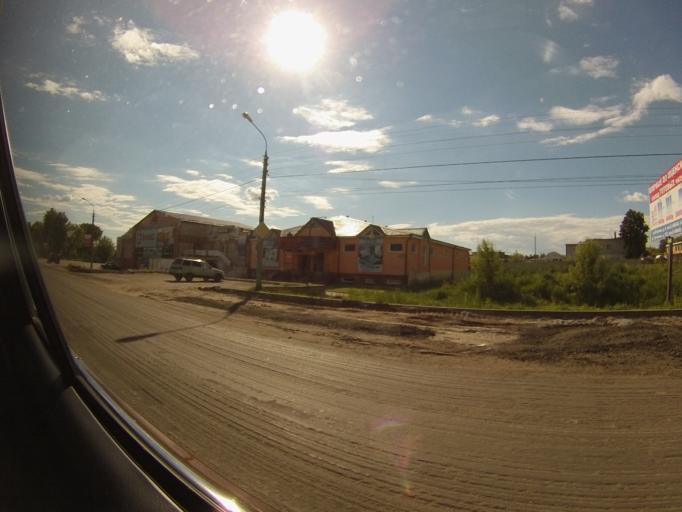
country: RU
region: Orjol
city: Mtsensk
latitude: 53.2852
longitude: 36.5885
